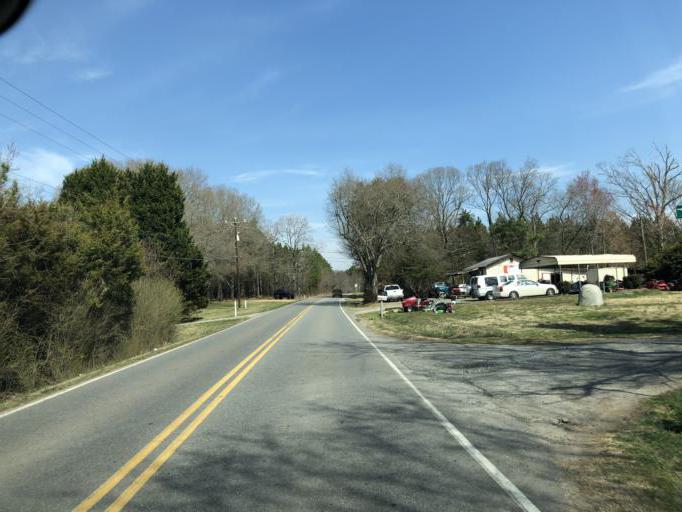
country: US
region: North Carolina
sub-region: Gaston County
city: Stanley
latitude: 35.3243
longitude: -81.1014
